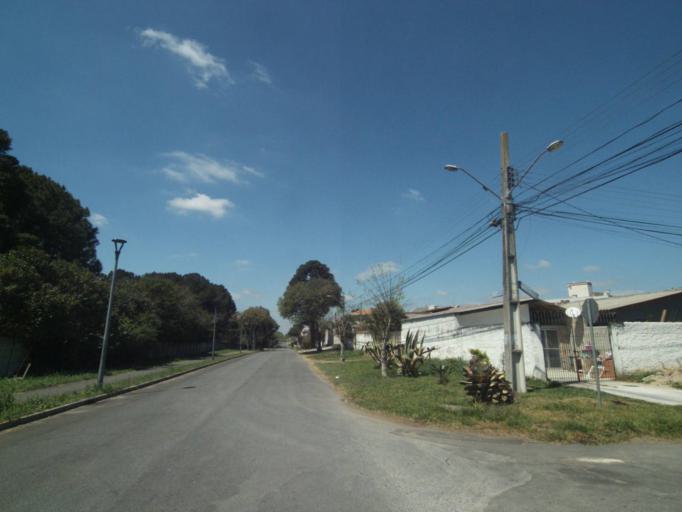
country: BR
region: Parana
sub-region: Sao Jose Dos Pinhais
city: Sao Jose dos Pinhais
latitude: -25.5104
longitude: -49.2387
